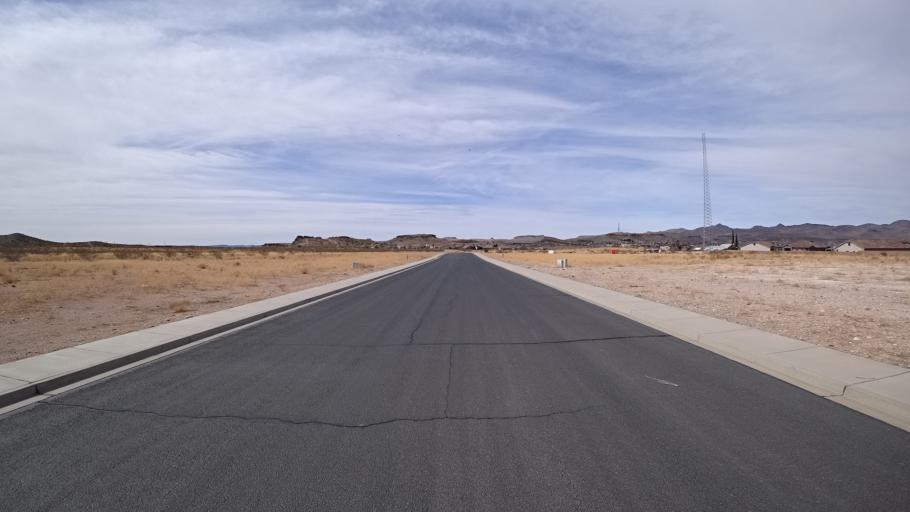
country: US
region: Arizona
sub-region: Mohave County
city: Kingman
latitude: 35.1886
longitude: -114.0184
